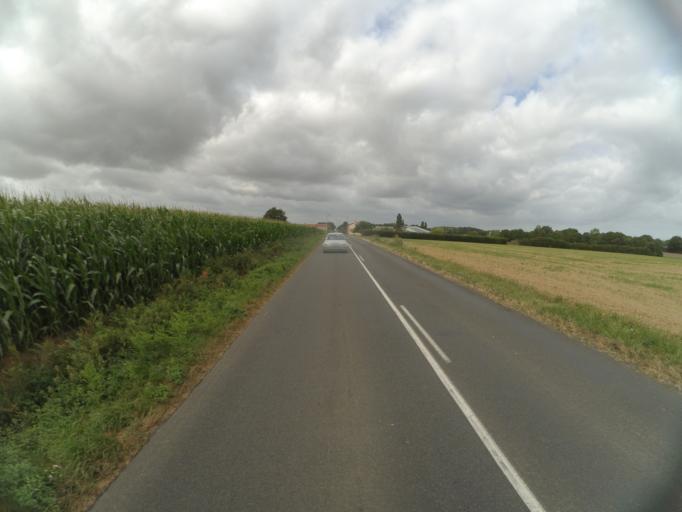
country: FR
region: Pays de la Loire
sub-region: Departement de Maine-et-Loire
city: Villedieu-la-Blouere
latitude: 47.1388
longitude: -1.0740
